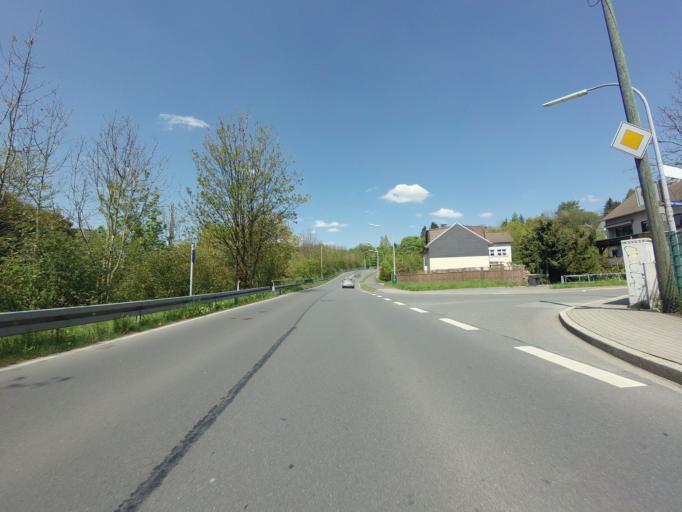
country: DE
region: North Rhine-Westphalia
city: Hemer
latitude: 51.3738
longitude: 7.7844
